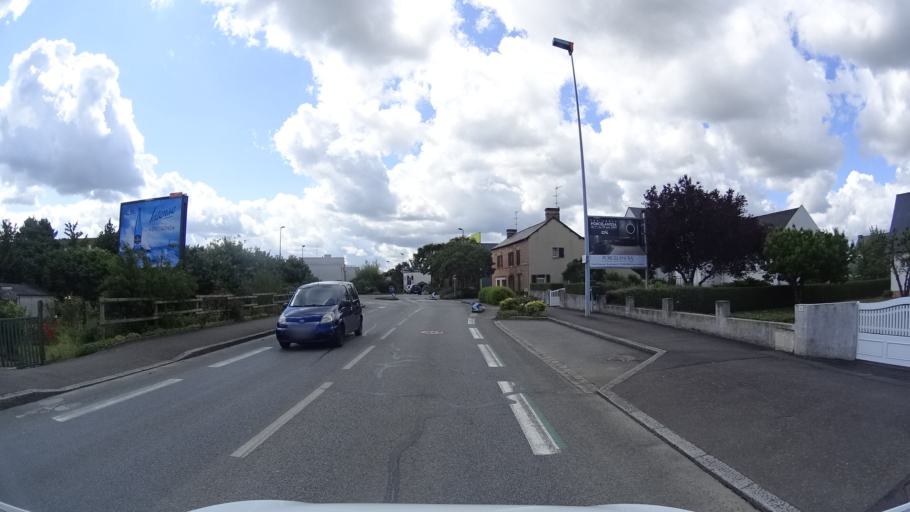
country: FR
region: Brittany
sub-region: Departement d'Ille-et-Vilaine
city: Chartres-de-Bretagne
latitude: 48.0356
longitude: -1.7126
